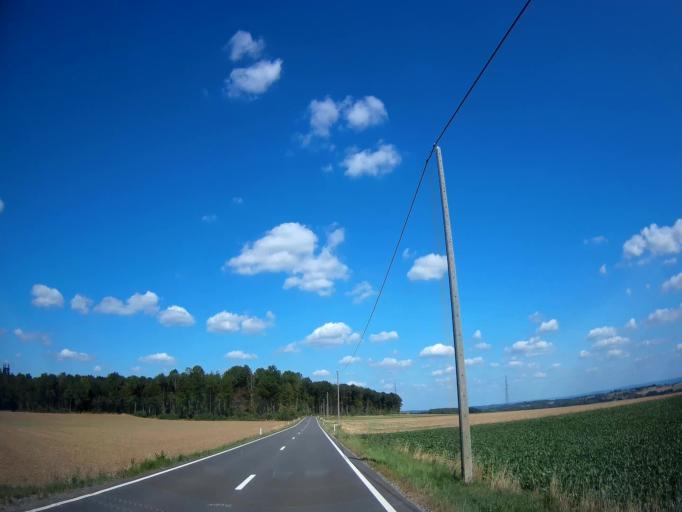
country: FR
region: Champagne-Ardenne
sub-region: Departement des Ardennes
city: Fromelennes
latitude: 50.1744
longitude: 4.9075
